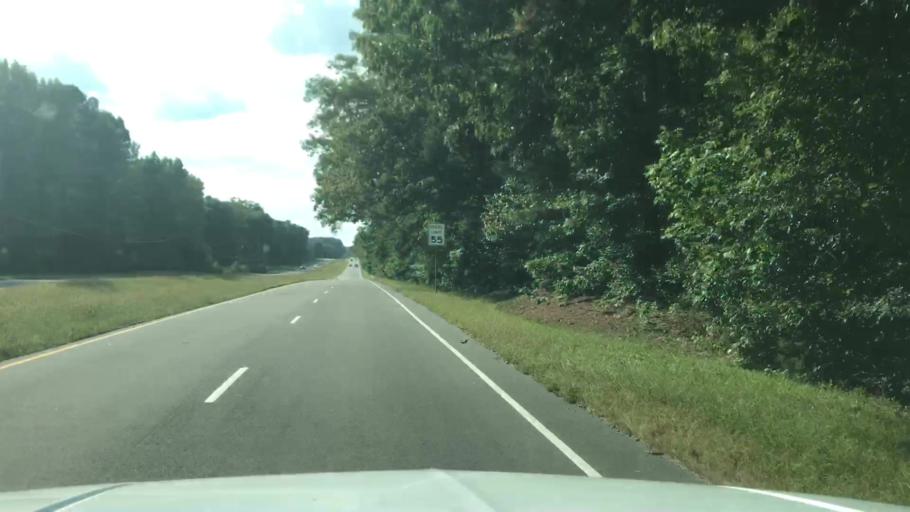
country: US
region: Virginia
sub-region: Henrico County
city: Short Pump
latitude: 37.5995
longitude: -77.6766
